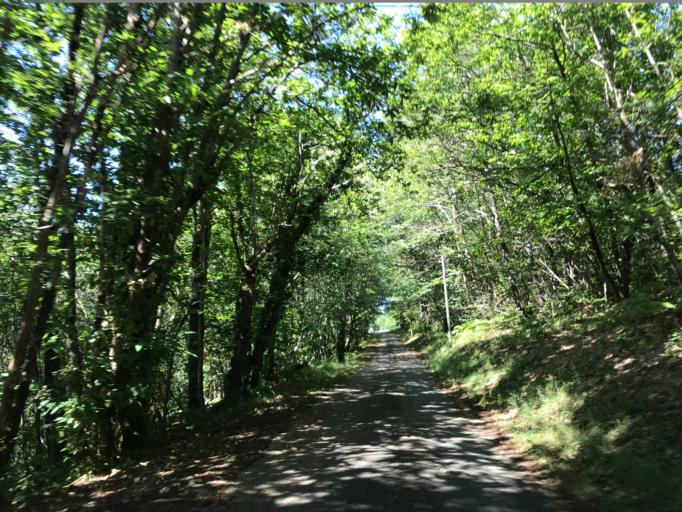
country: FR
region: Aquitaine
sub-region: Departement de la Dordogne
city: Sarlat-la-Caneda
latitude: 44.9109
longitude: 1.1689
